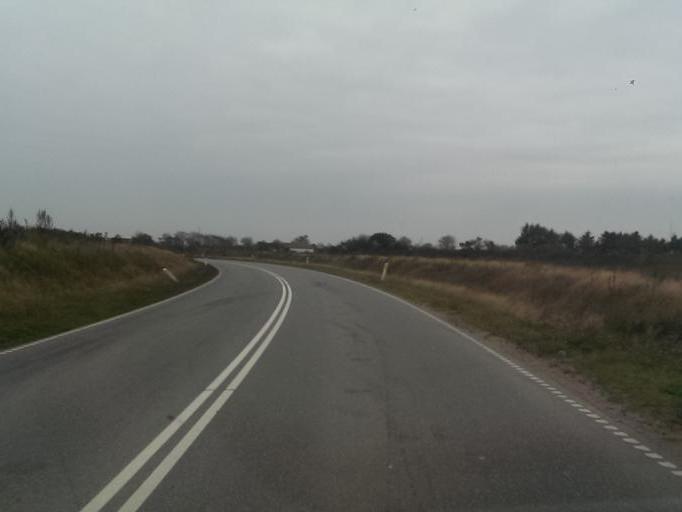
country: DK
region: South Denmark
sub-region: Esbjerg Kommune
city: Tjaereborg
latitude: 55.4658
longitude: 8.5569
